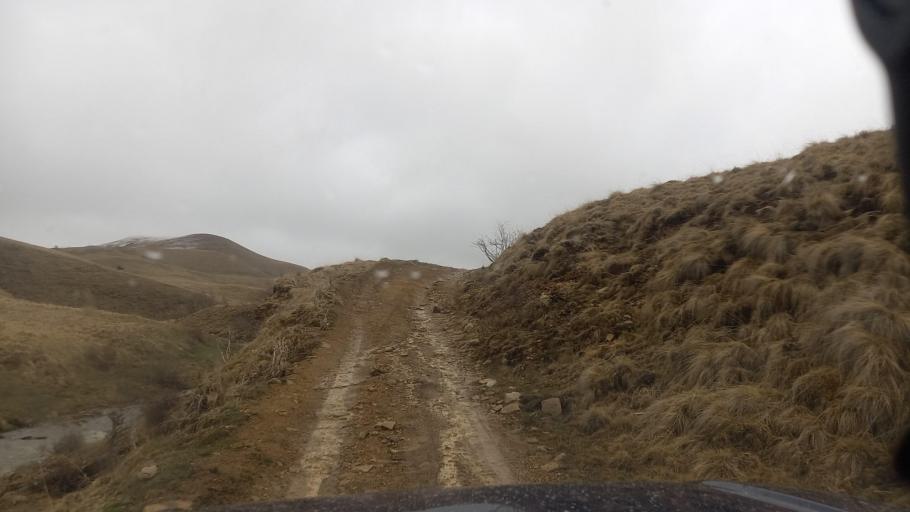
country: RU
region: Kabardino-Balkariya
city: Terskol
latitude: 43.5235
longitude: 42.4250
